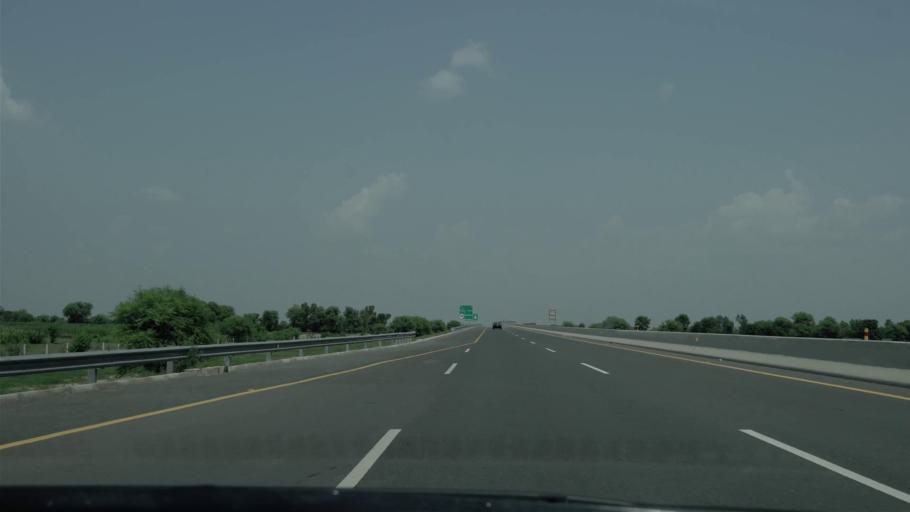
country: PK
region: Punjab
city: Gojra
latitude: 31.1869
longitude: 72.6448
